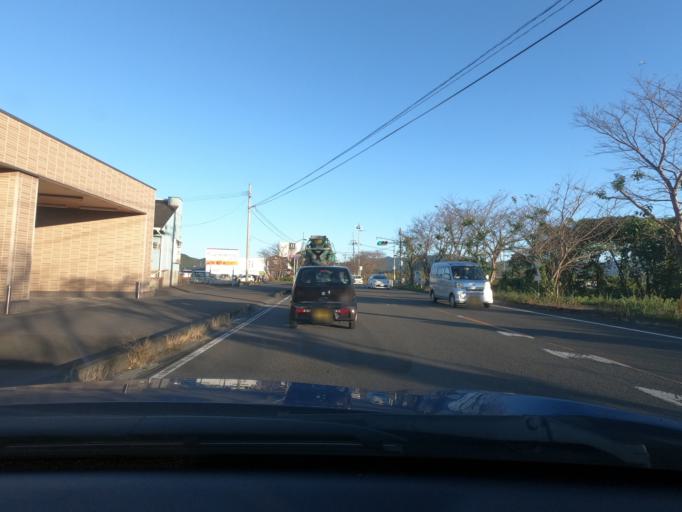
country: JP
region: Kagoshima
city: Satsumasendai
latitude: 31.8101
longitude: 130.3158
